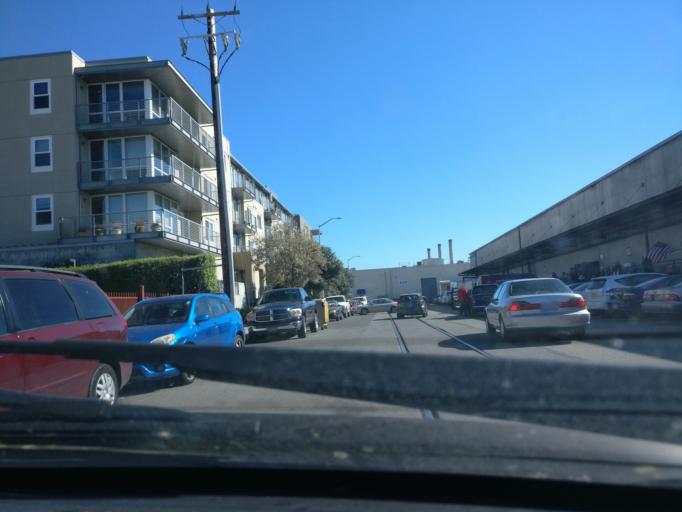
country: US
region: California
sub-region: Alameda County
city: Alameda
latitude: 37.7713
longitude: -122.2318
